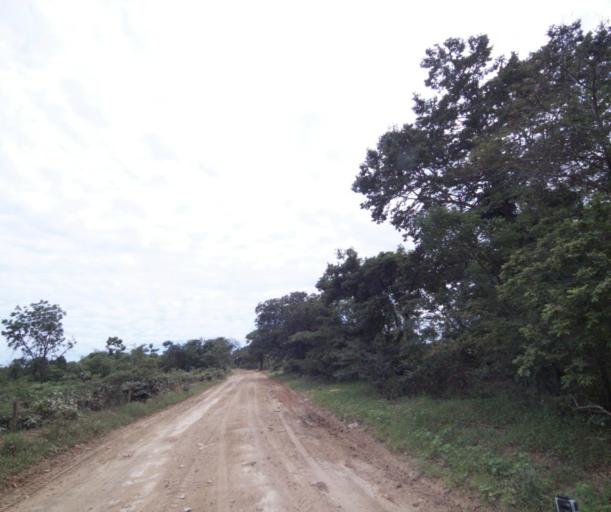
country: BR
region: Bahia
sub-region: Carinhanha
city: Carinhanha
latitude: -14.2264
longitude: -44.3009
